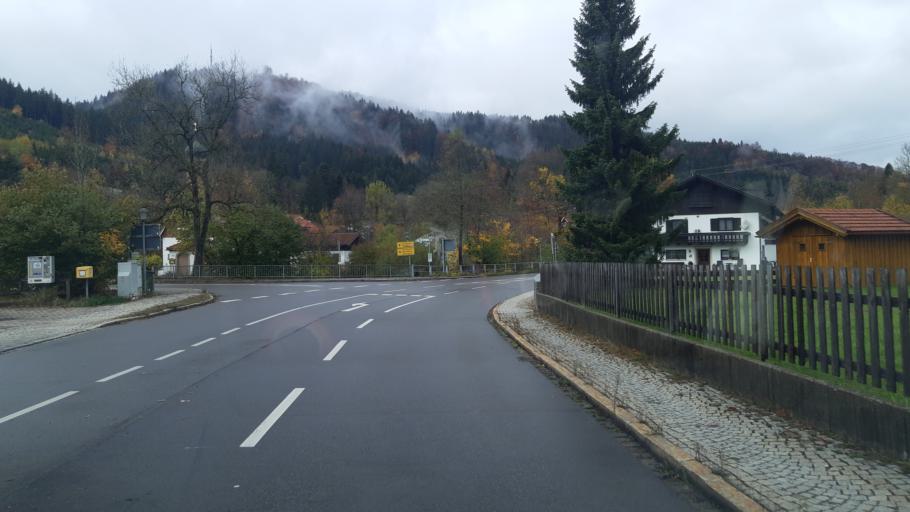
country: DE
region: Bavaria
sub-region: Swabia
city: Weitnau
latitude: 47.6410
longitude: 10.0938
